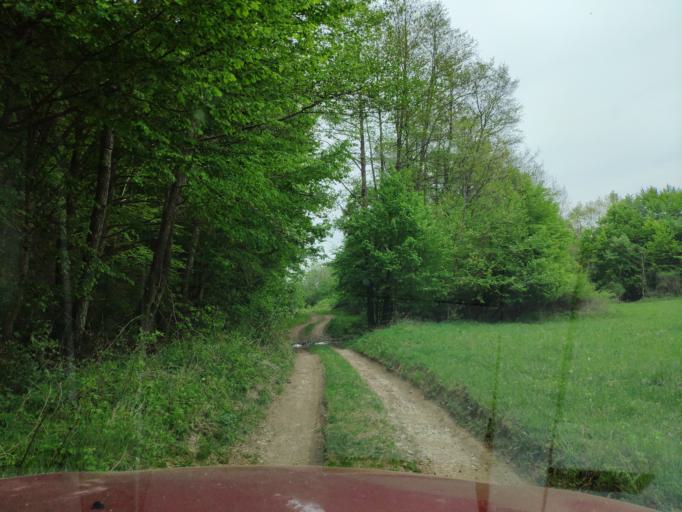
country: SK
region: Banskobystricky
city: Revuca
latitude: 48.5176
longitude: 20.1626
